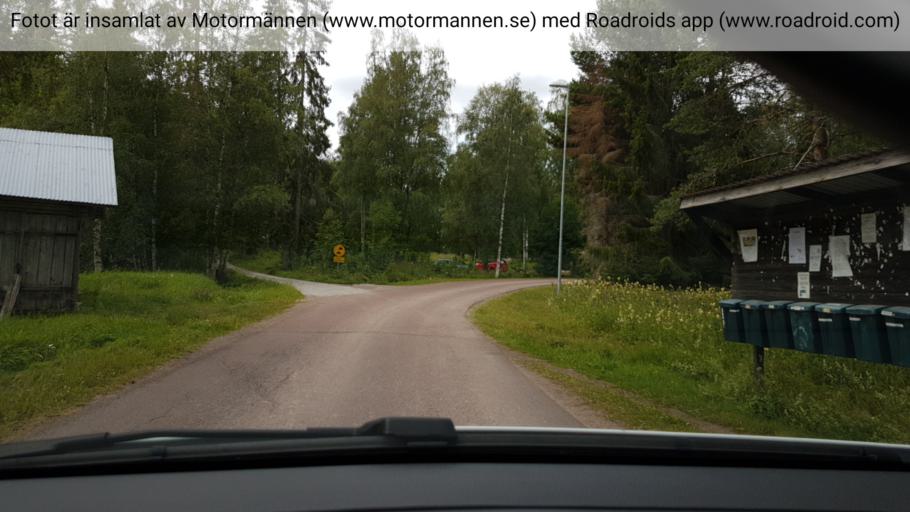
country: SE
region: Dalarna
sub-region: Rattviks Kommun
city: Raettvik
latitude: 60.9672
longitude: 15.1558
